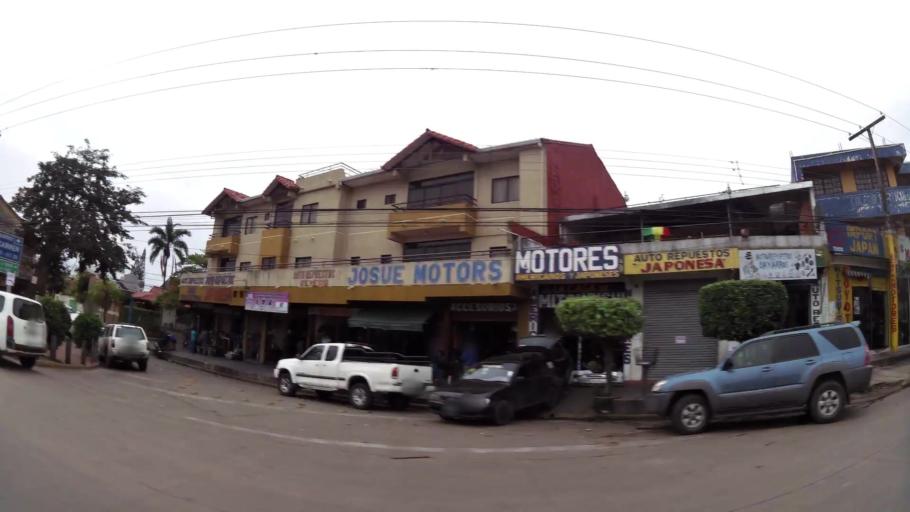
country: BO
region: Santa Cruz
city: Santa Cruz de la Sierra
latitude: -17.8098
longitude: -63.1926
